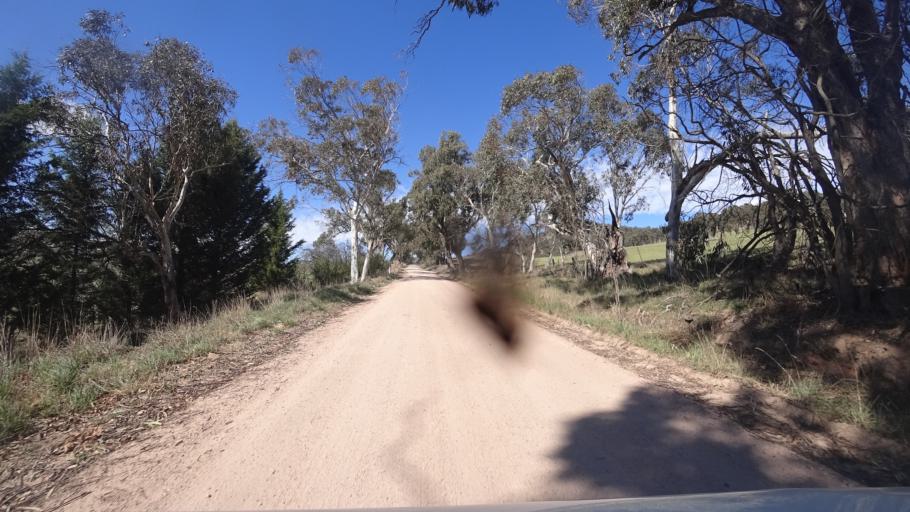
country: AU
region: New South Wales
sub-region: Lithgow
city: Portland
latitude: -33.5236
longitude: 149.9357
